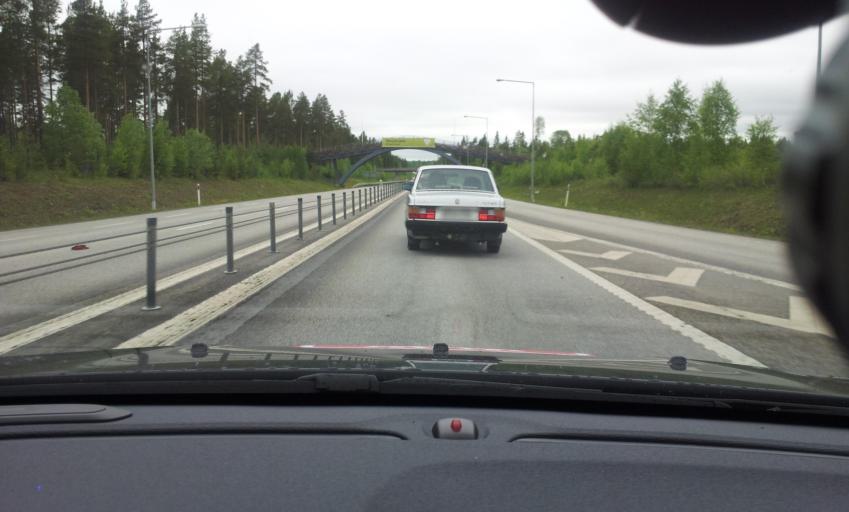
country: SE
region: Jaemtland
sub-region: OEstersunds Kommun
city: Ostersund
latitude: 63.2044
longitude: 14.6747
